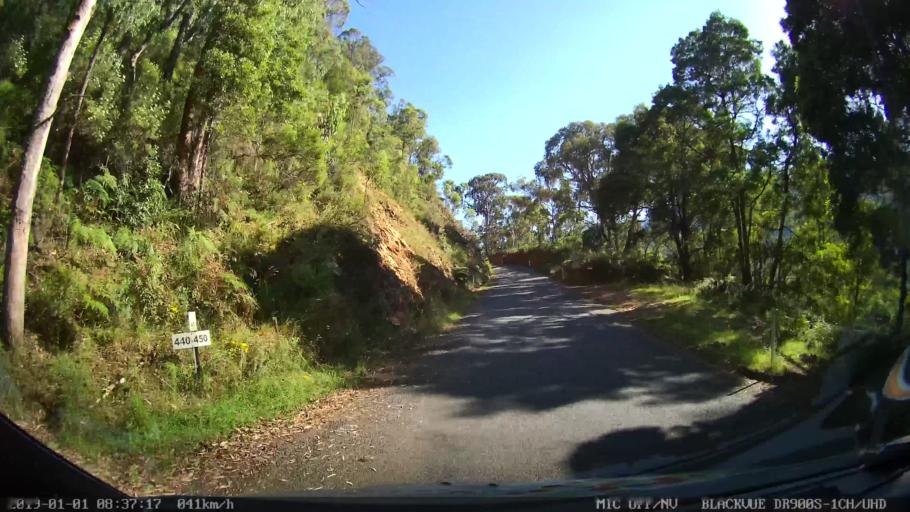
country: AU
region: New South Wales
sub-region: Snowy River
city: Jindabyne
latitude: -36.3392
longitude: 148.1957
